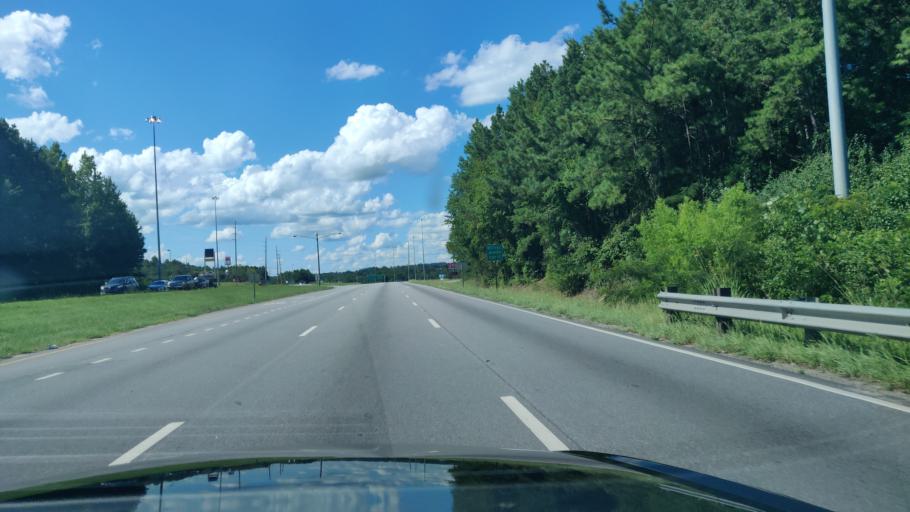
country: US
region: Alabama
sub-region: Russell County
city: Phenix City
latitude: 32.4782
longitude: -85.0303
